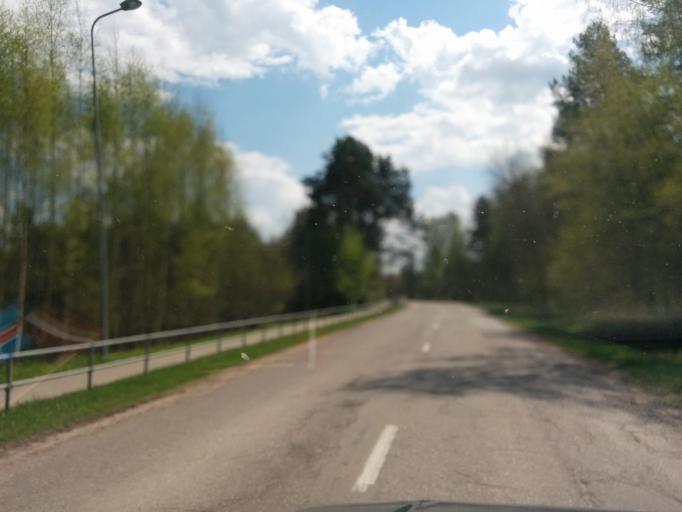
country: LV
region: Ozolnieku
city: Ozolnieki
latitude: 56.6149
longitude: 23.7830
